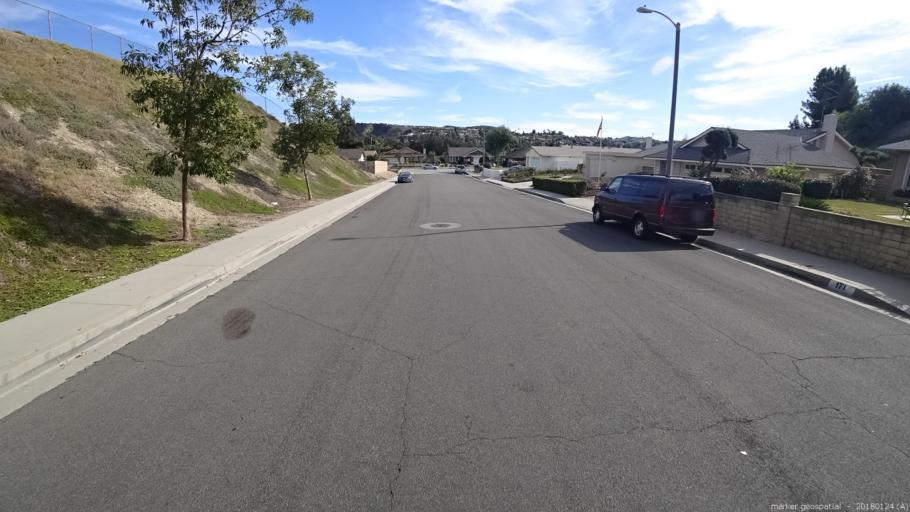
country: US
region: California
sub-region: Los Angeles County
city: Diamond Bar
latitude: 34.0197
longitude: -117.8176
